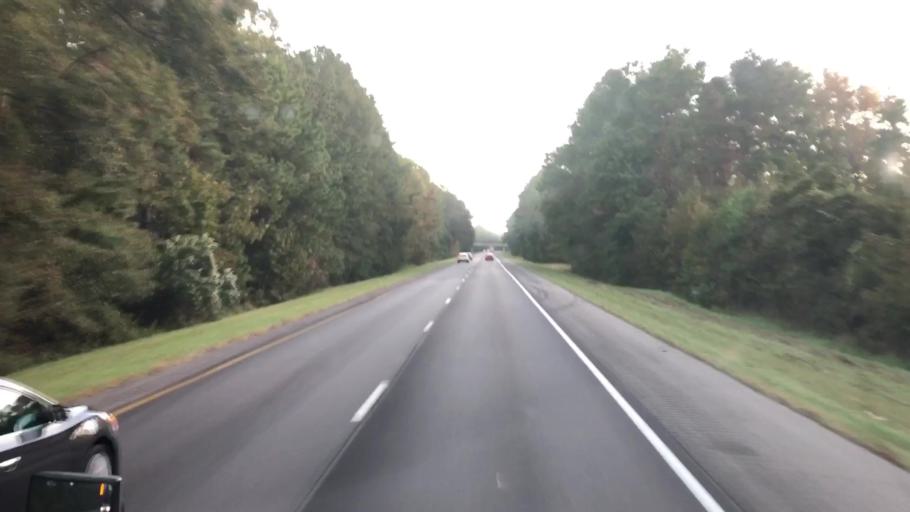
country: US
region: South Carolina
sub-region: Clarendon County
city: Manning
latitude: 33.5627
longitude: -80.3939
